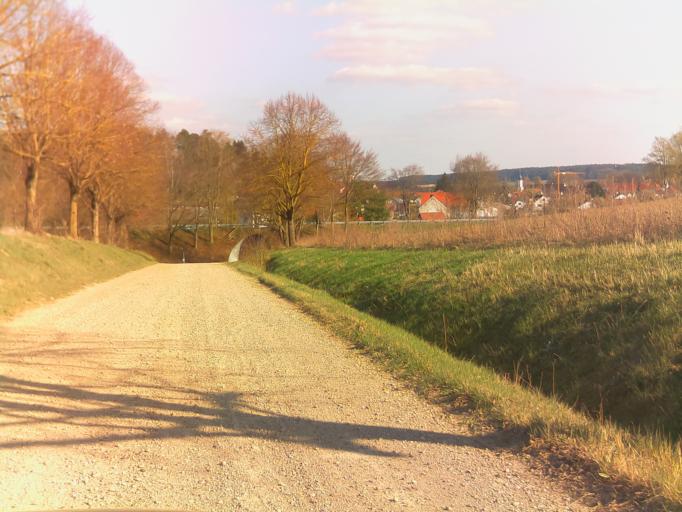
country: DE
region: Bavaria
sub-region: Swabia
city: Pottmes
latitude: 48.5887
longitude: 11.0790
